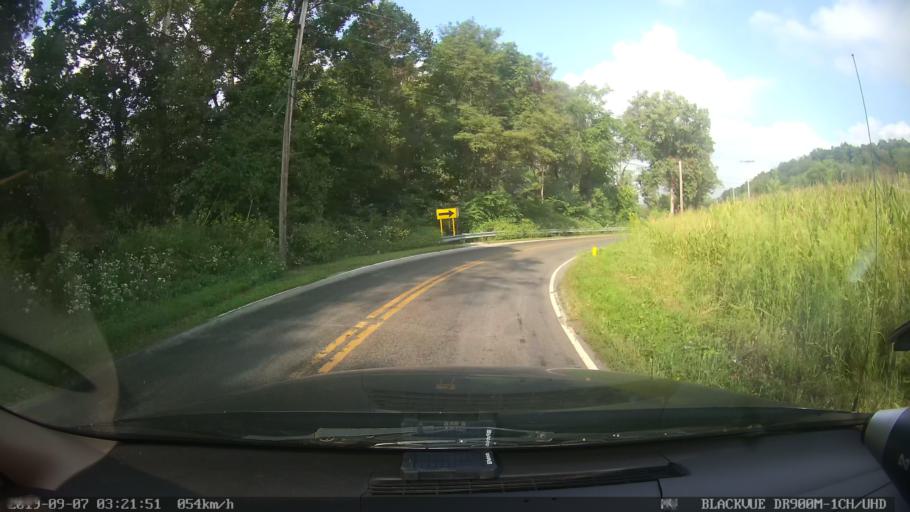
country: US
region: Ohio
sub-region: Licking County
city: Granville
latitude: 40.1160
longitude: -82.4562
